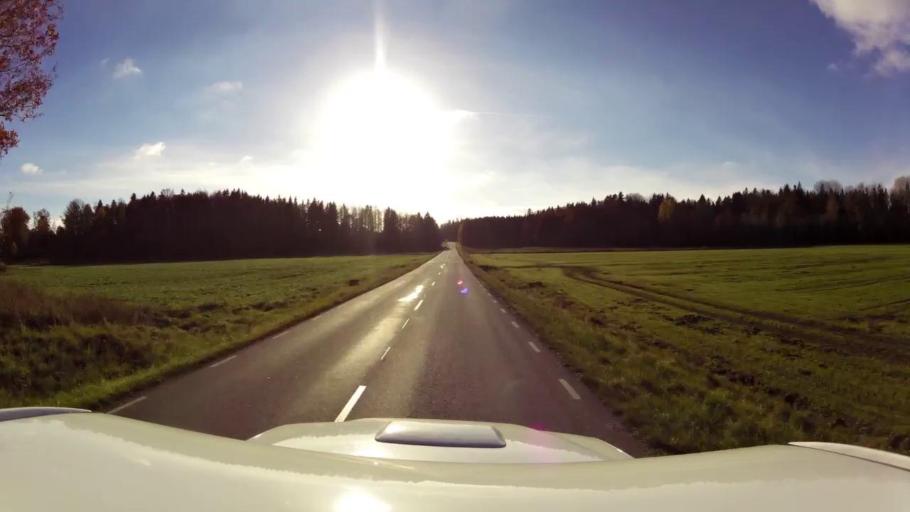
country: SE
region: OEstergoetland
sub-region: Linkopings Kommun
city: Malmslatt
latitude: 58.3256
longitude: 15.5046
